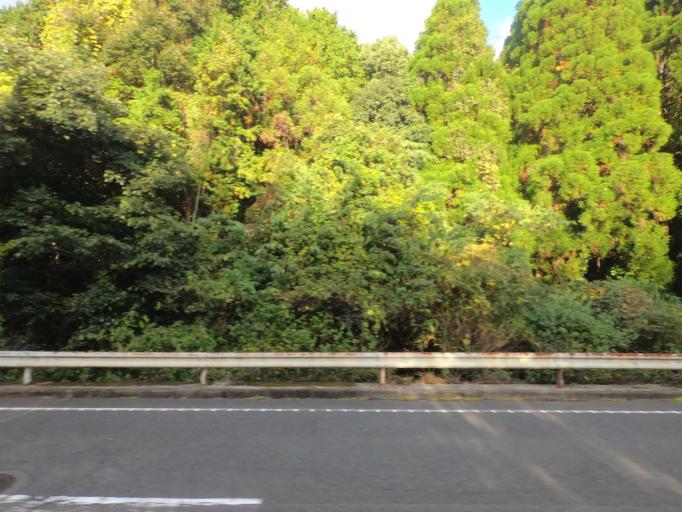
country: JP
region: Kumamoto
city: Minamata
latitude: 32.2434
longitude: 130.4796
